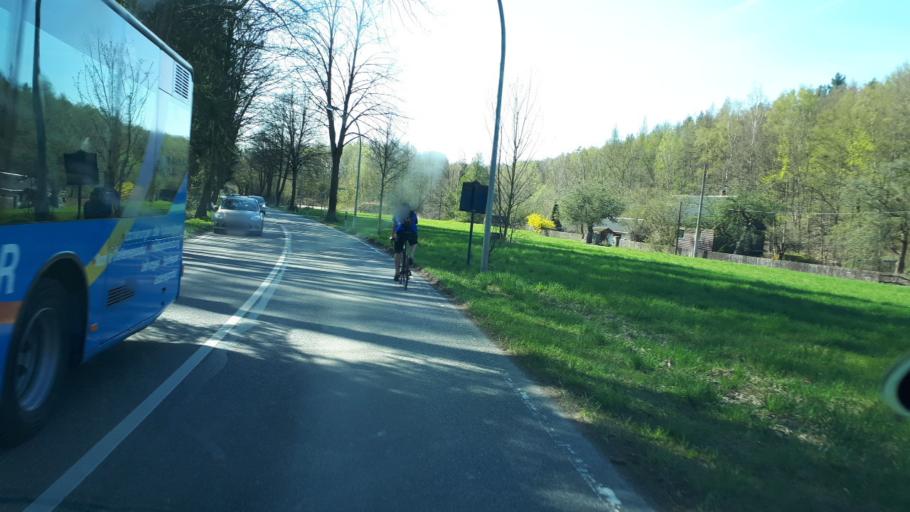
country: DE
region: Saxony
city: Chemnitz
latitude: 50.7837
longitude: 12.9696
